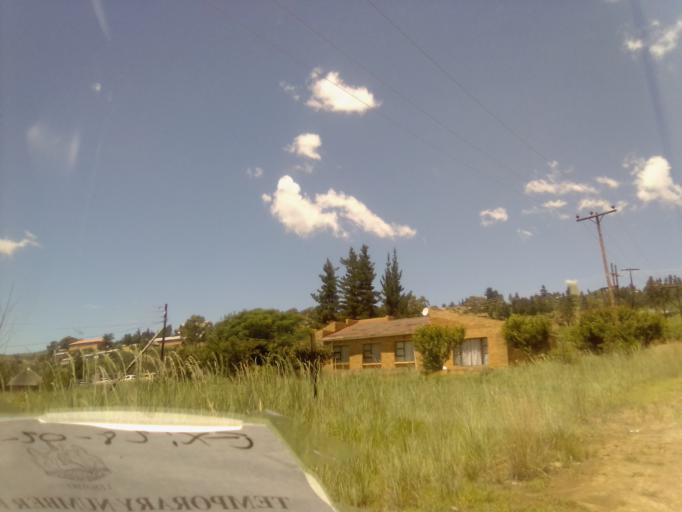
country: LS
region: Qacha's Nek
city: Qacha's Nek
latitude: -30.0906
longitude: 28.6431
